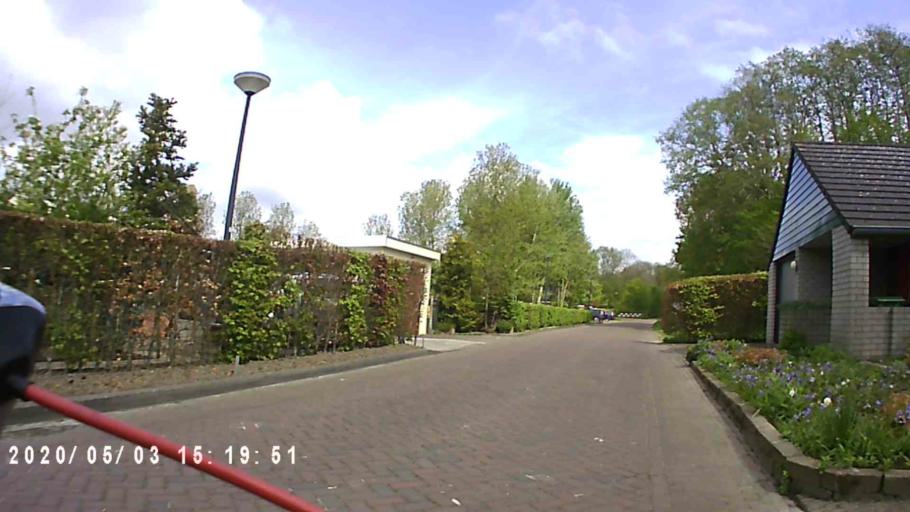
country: NL
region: Groningen
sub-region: Gemeente Winsum
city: Winsum
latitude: 53.3614
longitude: 6.4637
